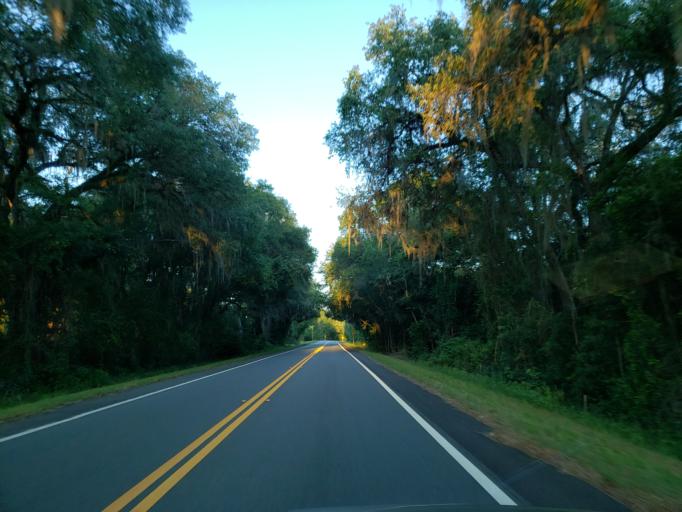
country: US
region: Florida
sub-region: Madison County
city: Madison
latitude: 30.5927
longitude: -83.2463
